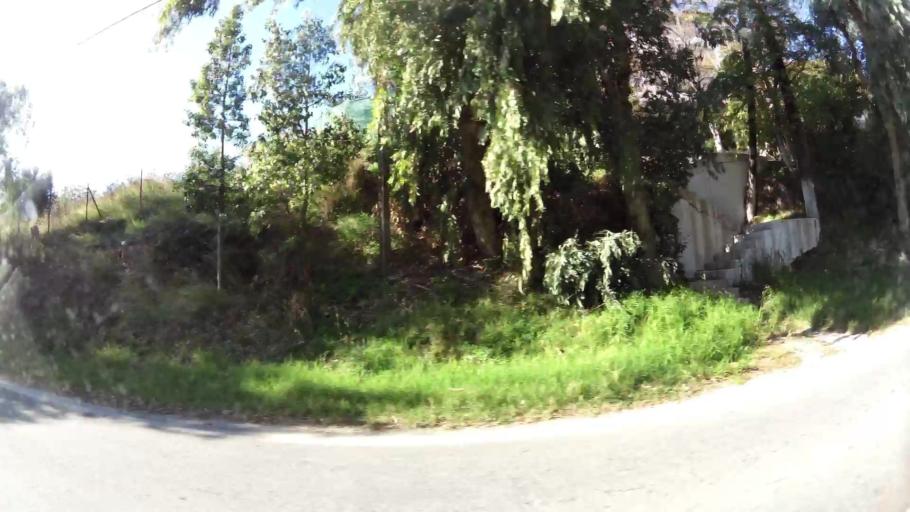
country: GR
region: Attica
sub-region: Nomarchia Athinas
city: Penteli
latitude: 38.0442
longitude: 23.8834
